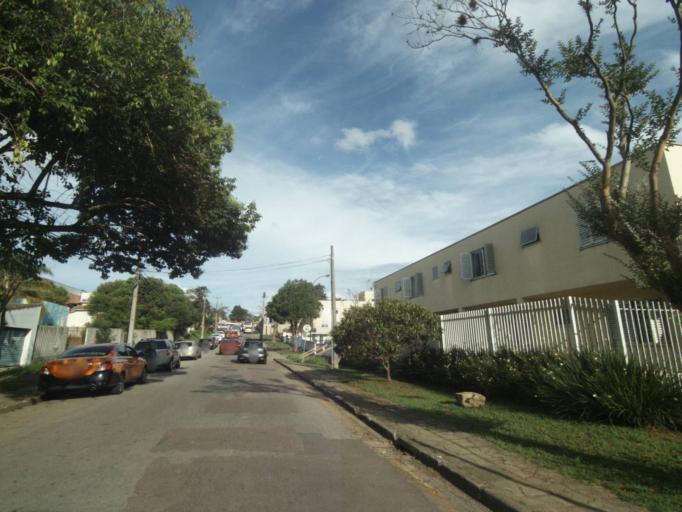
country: BR
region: Parana
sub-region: Curitiba
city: Curitiba
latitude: -25.4455
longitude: -49.3065
